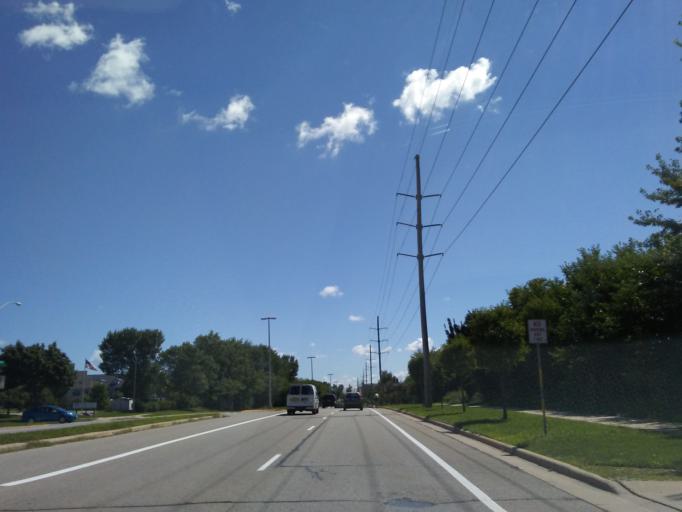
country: US
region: Wisconsin
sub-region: Dane County
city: Verona
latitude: 43.0157
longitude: -89.4974
